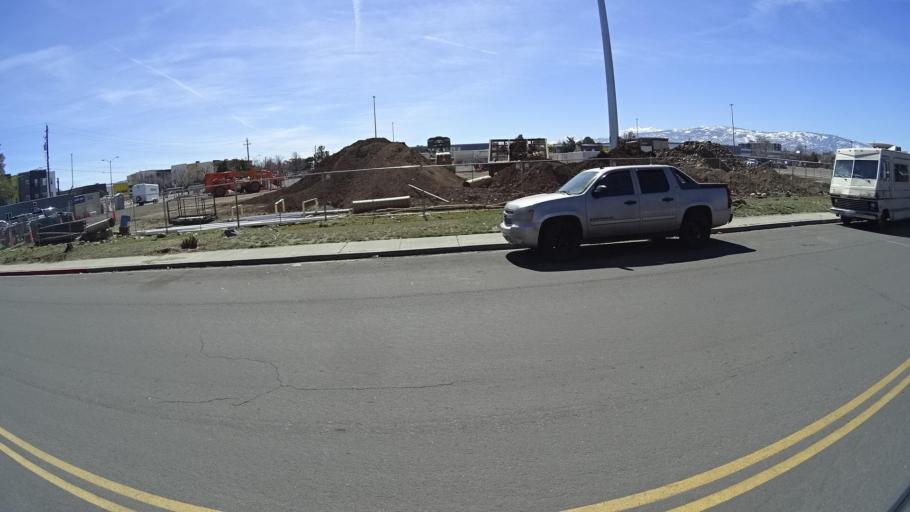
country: US
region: Nevada
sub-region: Washoe County
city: Sparks
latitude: 39.5476
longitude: -119.7763
